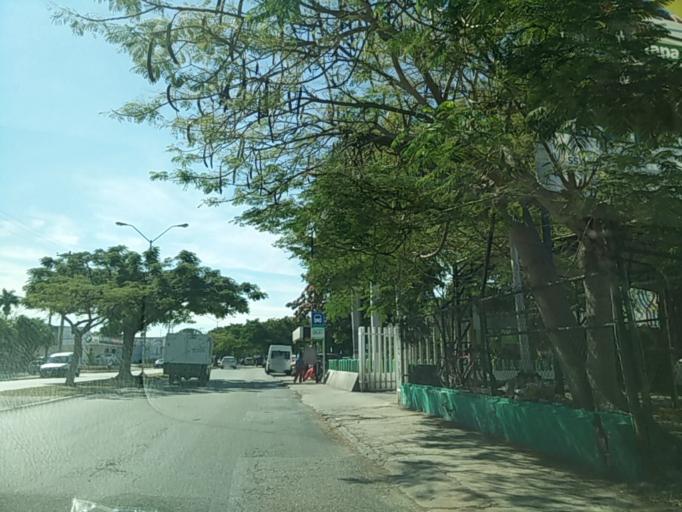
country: MX
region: Yucatan
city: Merida
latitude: 20.9889
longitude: -89.6087
